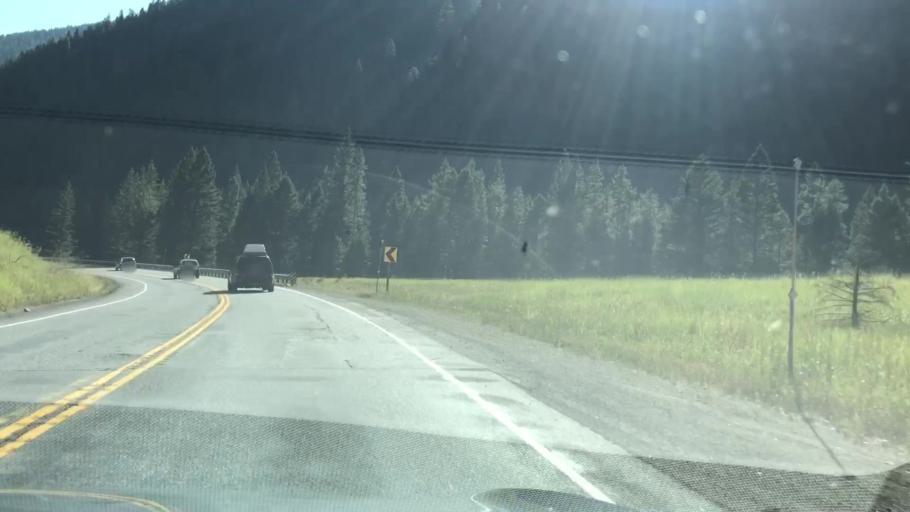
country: US
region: Montana
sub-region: Gallatin County
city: Big Sky
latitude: 45.3759
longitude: -111.1751
